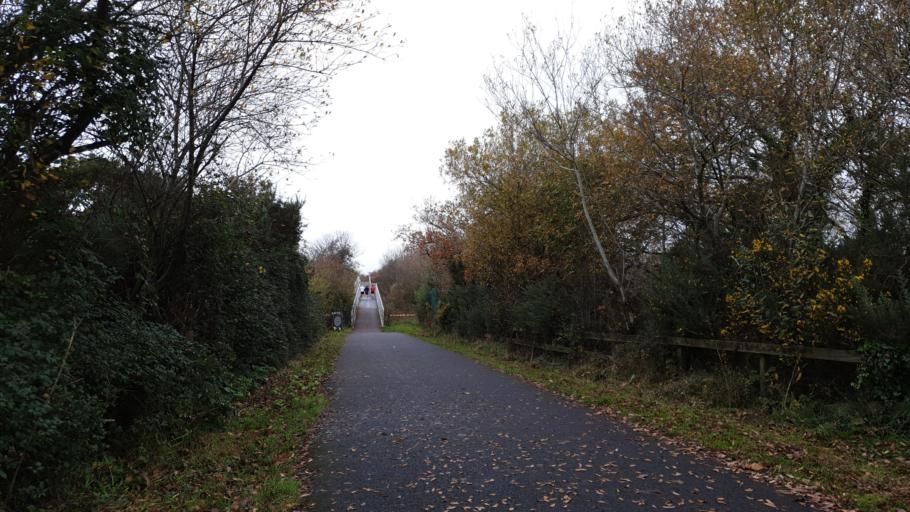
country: IE
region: Munster
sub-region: County Cork
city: Passage West
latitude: 51.8817
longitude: -8.4023
